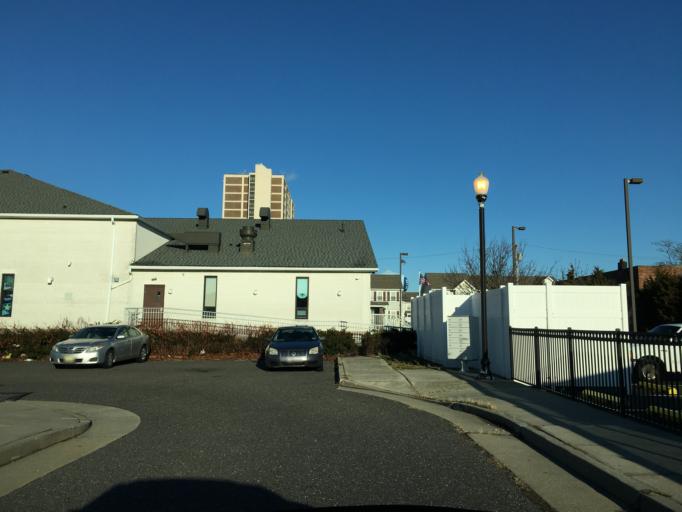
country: US
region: New Jersey
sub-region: Atlantic County
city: Atlantic City
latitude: 39.3666
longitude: -74.4240
